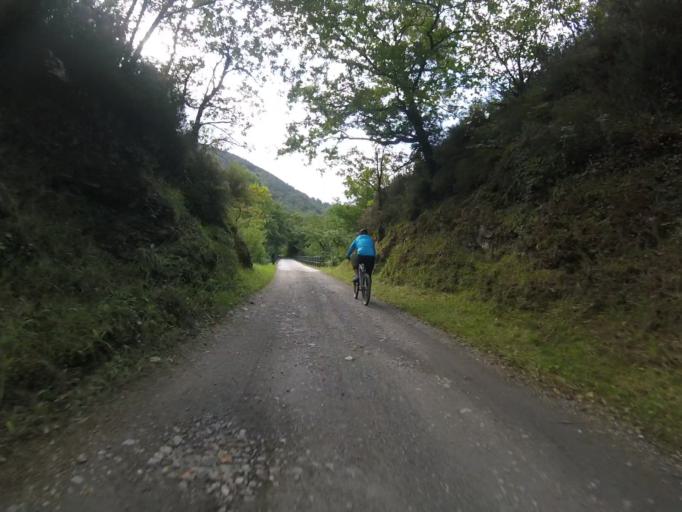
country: ES
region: Basque Country
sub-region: Provincia de Guipuzcoa
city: Berastegui
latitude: 43.1273
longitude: -1.9377
